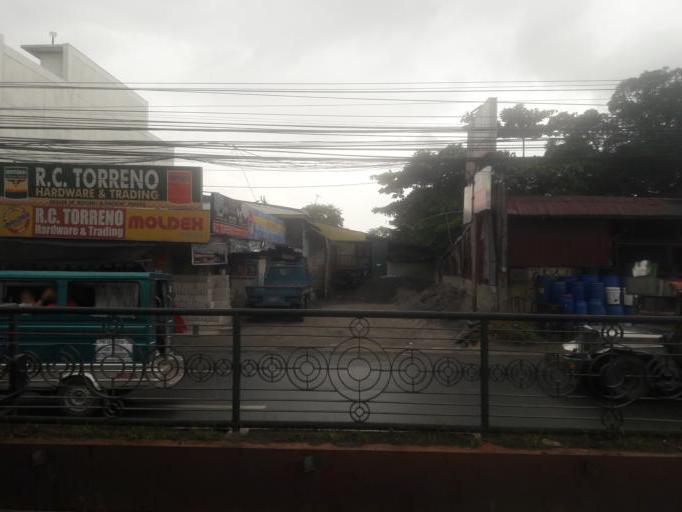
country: PH
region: Calabarzon
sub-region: Province of Cavite
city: Imus
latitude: 14.4307
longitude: 120.9460
